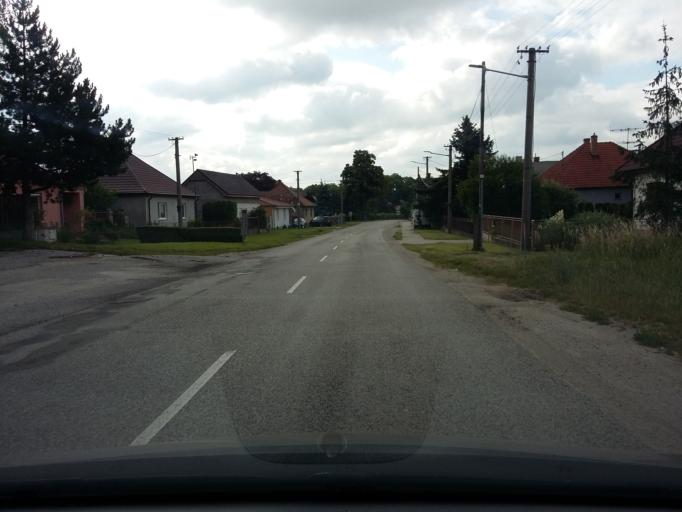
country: SK
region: Trnavsky
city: Smolenice
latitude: 48.5317
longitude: 17.4532
